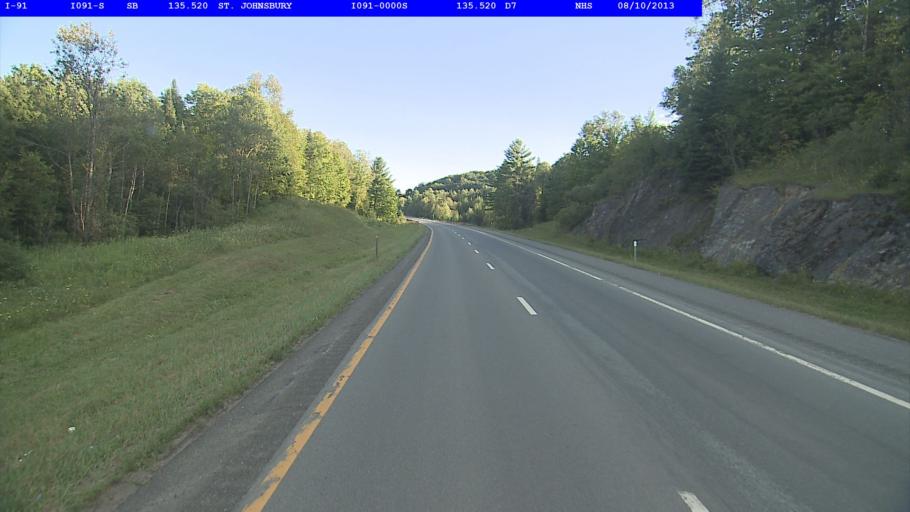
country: US
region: Vermont
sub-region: Caledonia County
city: Lyndon
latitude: 44.4968
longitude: -72.0223
